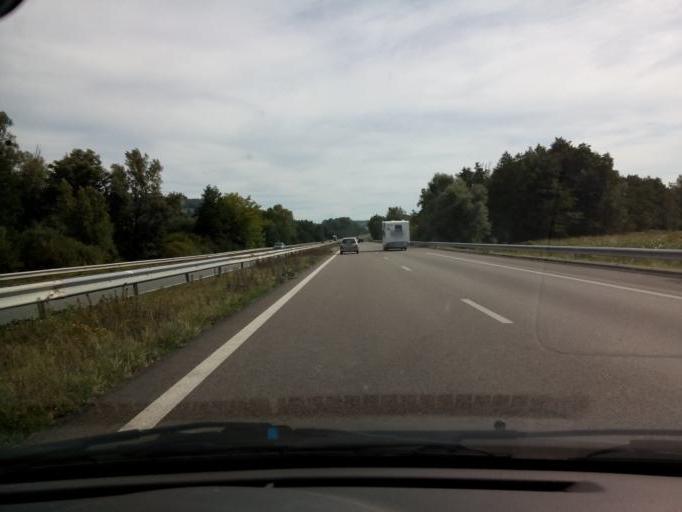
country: FR
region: Rhone-Alpes
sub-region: Departement de l'Isere
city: Saint-Victor-de-Cessieu
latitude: 45.4956
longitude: 5.3991
